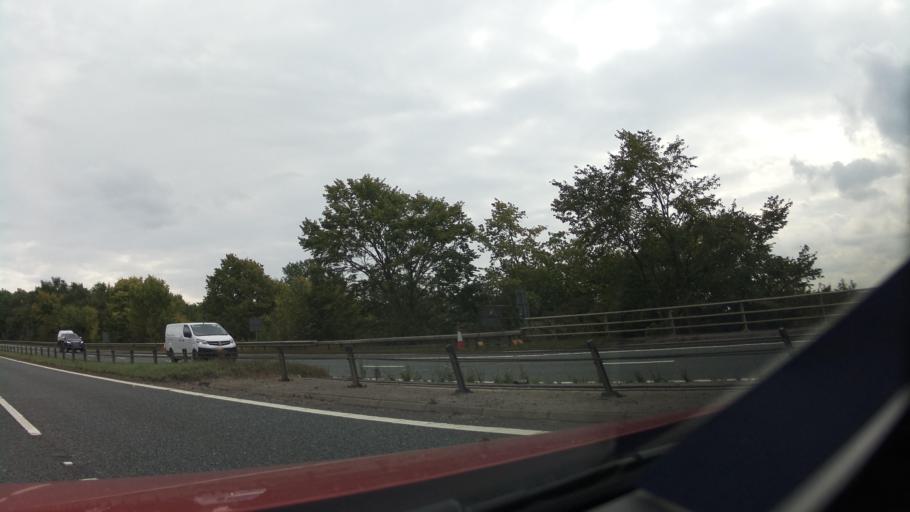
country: GB
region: England
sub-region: County Durham
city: Chester-le-Street
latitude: 54.8616
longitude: -1.5597
